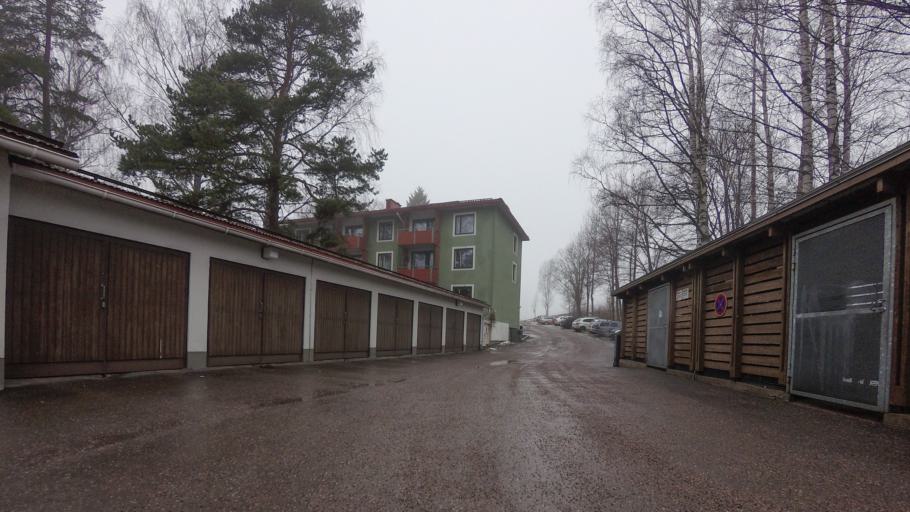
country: FI
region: Uusimaa
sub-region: Helsinki
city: Vantaa
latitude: 60.2082
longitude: 25.0466
